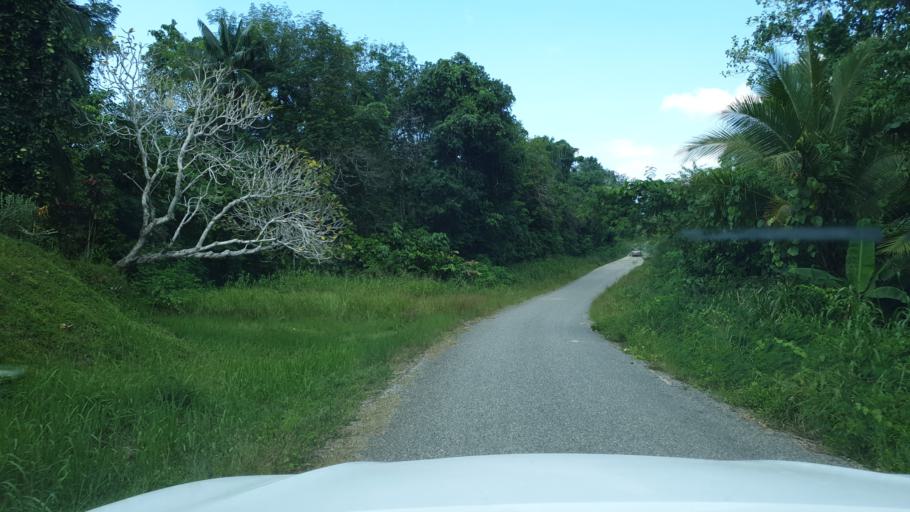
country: PG
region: East Sepik
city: Angoram
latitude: -3.9547
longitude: 144.0347
